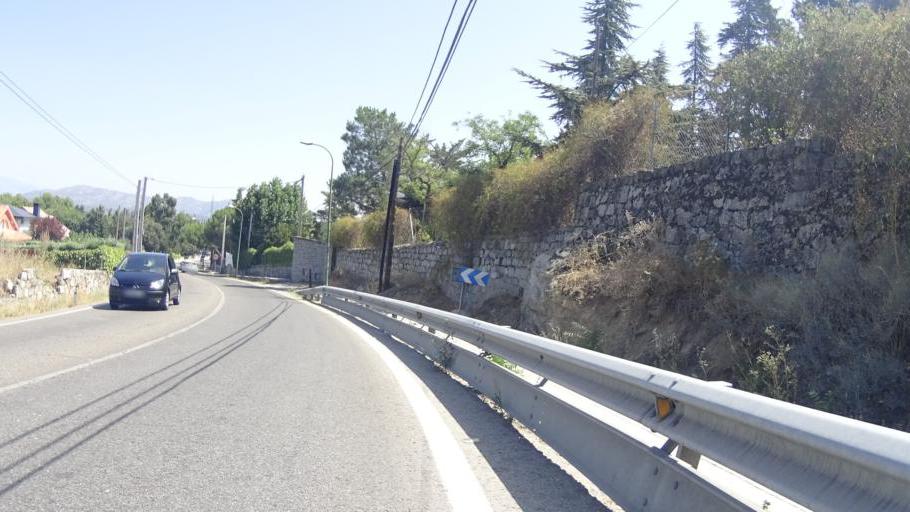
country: ES
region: Madrid
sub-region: Provincia de Madrid
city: Galapagar
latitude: 40.5708
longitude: -4.0095
